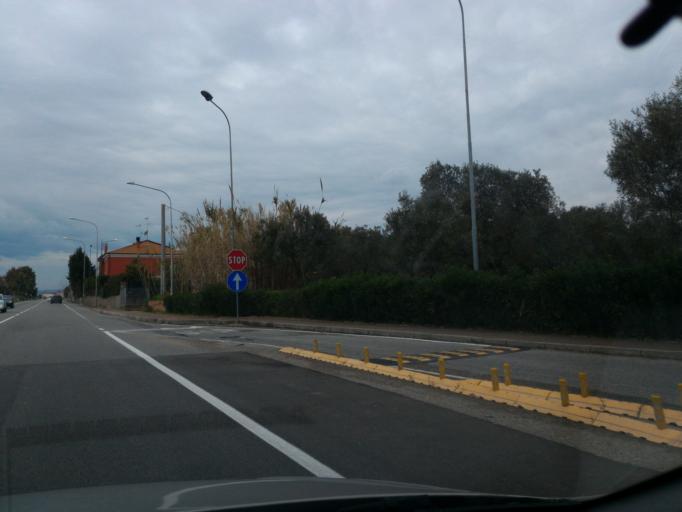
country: IT
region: Calabria
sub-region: Provincia di Catanzaro
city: Barone
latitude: 38.8413
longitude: 16.6465
